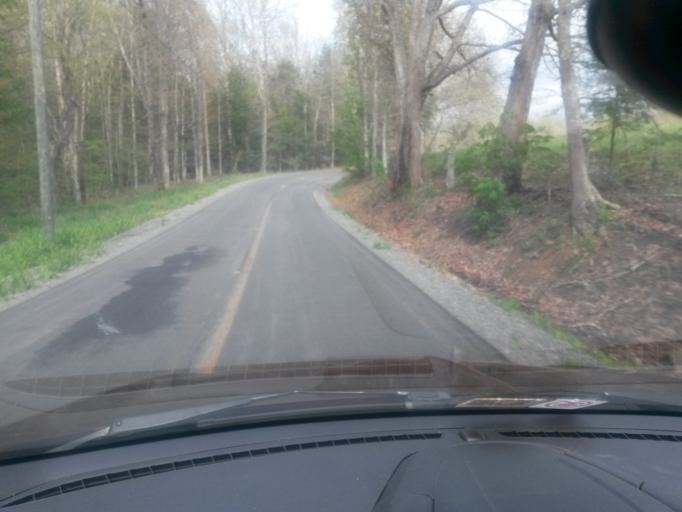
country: US
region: West Virginia
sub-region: Pocahontas County
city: Marlinton
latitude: 38.1104
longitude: -80.2210
